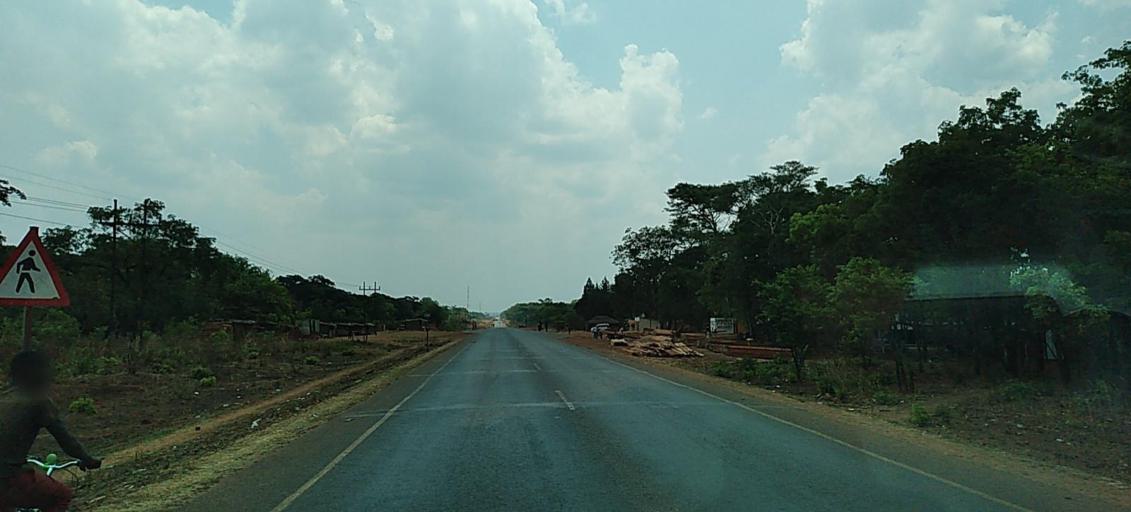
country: ZM
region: Copperbelt
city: Kalulushi
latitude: -12.8425
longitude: 28.0059
